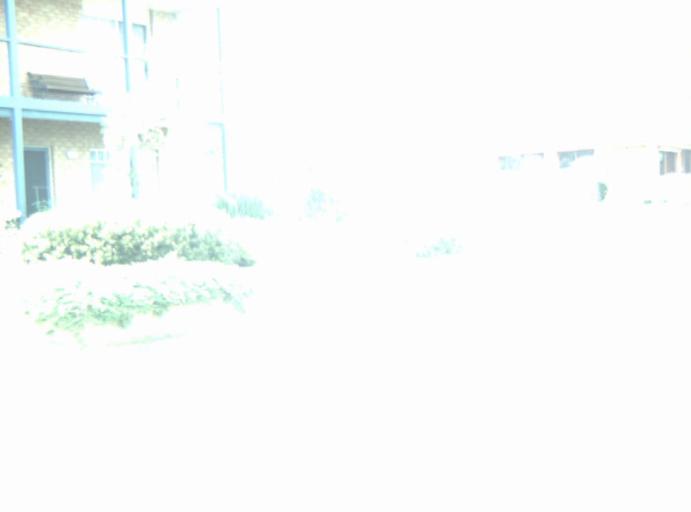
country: AU
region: Victoria
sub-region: Greater Geelong
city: Clifton Springs
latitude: -38.1439
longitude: 144.5765
